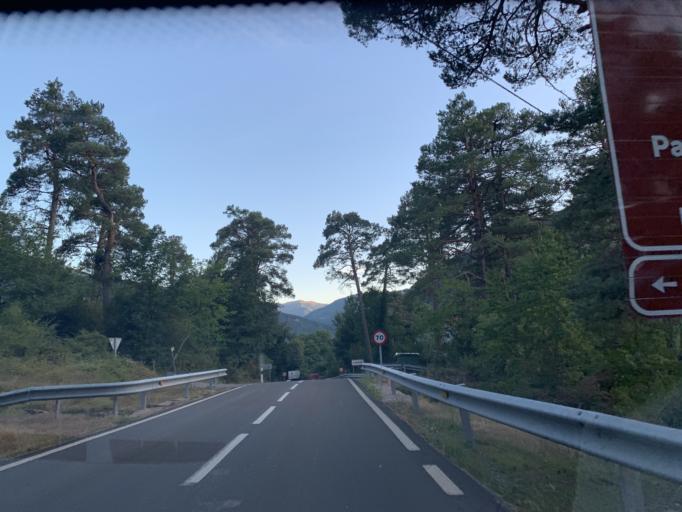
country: ES
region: Aragon
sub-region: Provincia de Huesca
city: Broto
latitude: 42.5807
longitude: -0.1150
